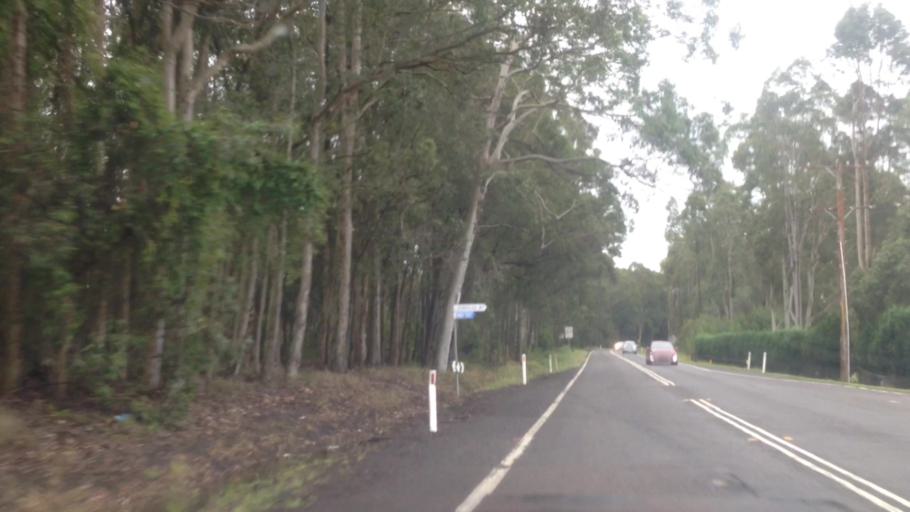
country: AU
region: New South Wales
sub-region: Wyong Shire
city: Little Jilliby
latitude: -33.2552
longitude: 151.3973
